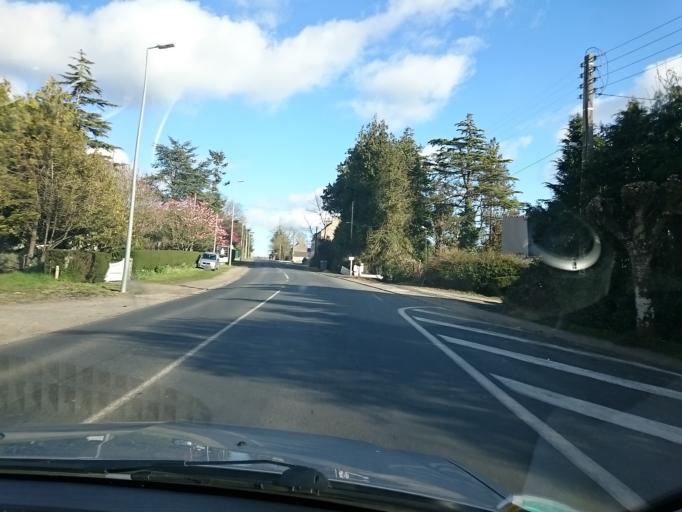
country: FR
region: Lower Normandy
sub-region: Departement de la Manche
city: Valognes
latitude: 49.5033
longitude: -1.4615
